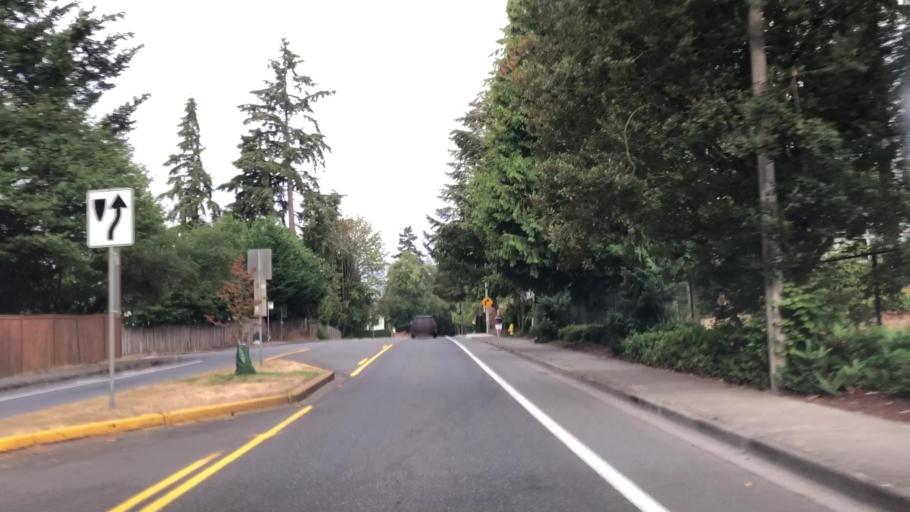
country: US
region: Washington
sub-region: King County
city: Kirkland
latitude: 47.6682
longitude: -122.1809
